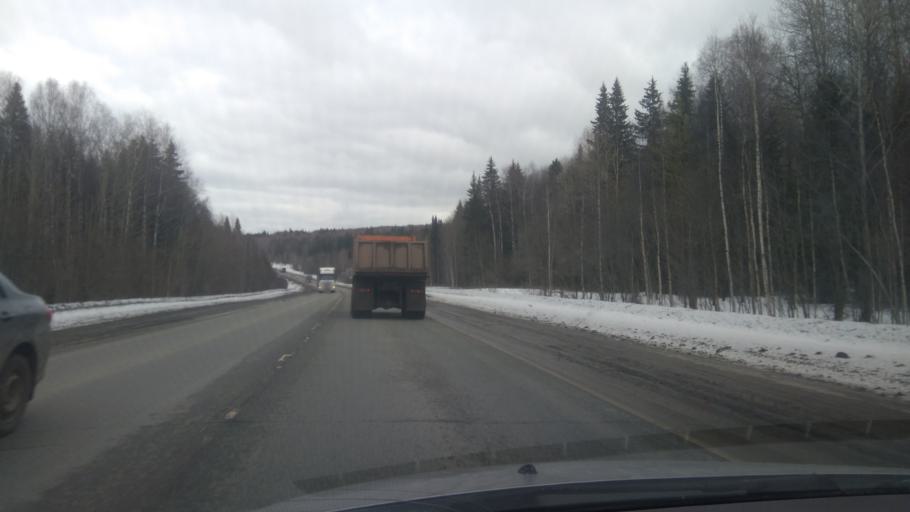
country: RU
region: Sverdlovsk
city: Bisert'
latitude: 56.8281
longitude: 59.1014
